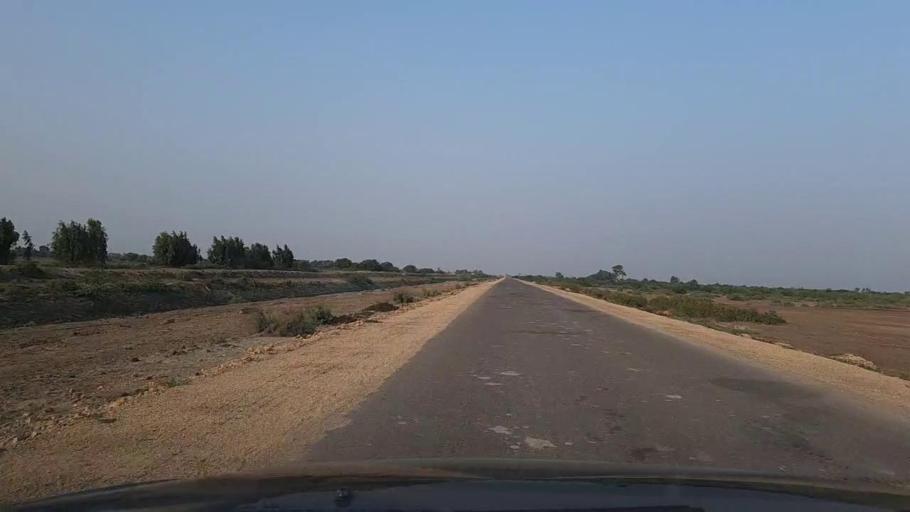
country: PK
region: Sindh
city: Mirpur Sakro
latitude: 24.4760
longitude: 67.8026
